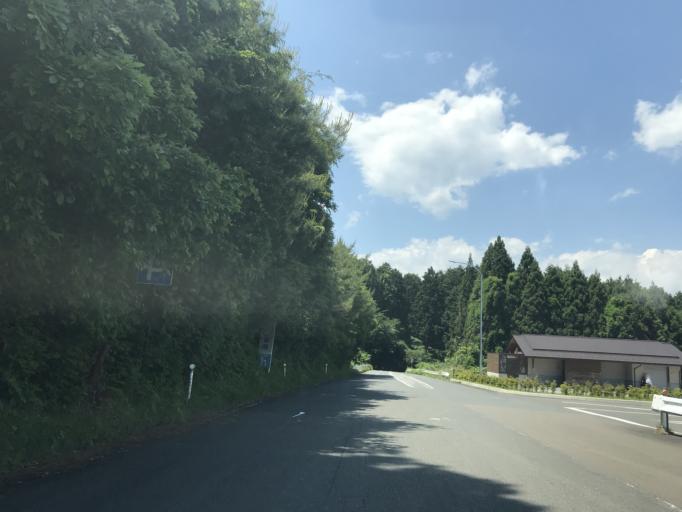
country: JP
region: Miyagi
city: Matsushima
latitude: 38.3671
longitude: 141.0517
